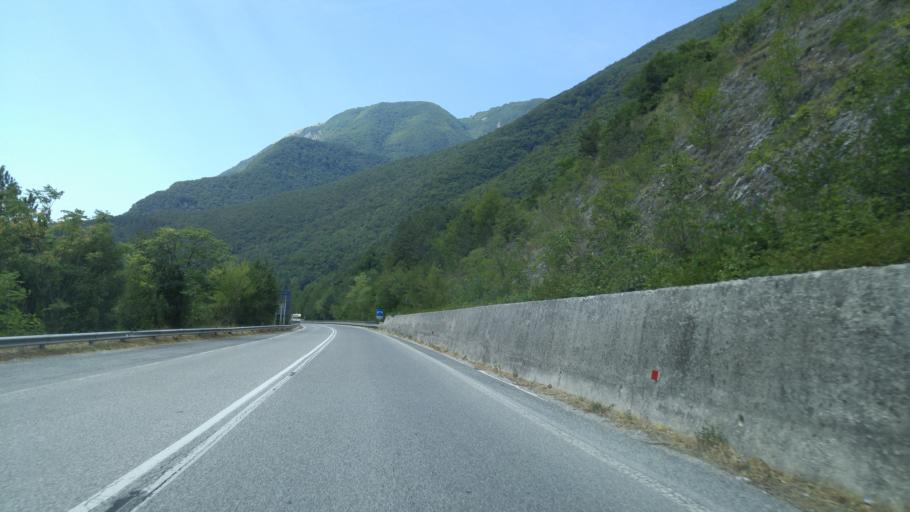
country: IT
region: The Marches
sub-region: Provincia di Pesaro e Urbino
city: Cagli
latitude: 43.5312
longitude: 12.6444
